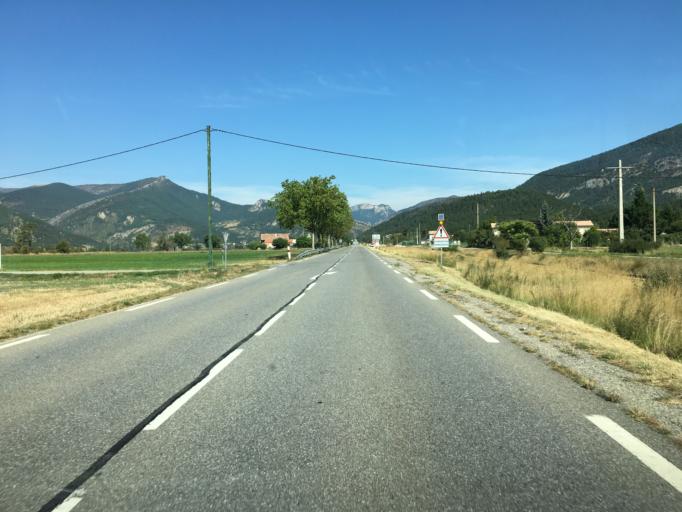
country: FR
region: Provence-Alpes-Cote d'Azur
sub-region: Departement des Hautes-Alpes
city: Serres
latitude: 44.4022
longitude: 5.7326
